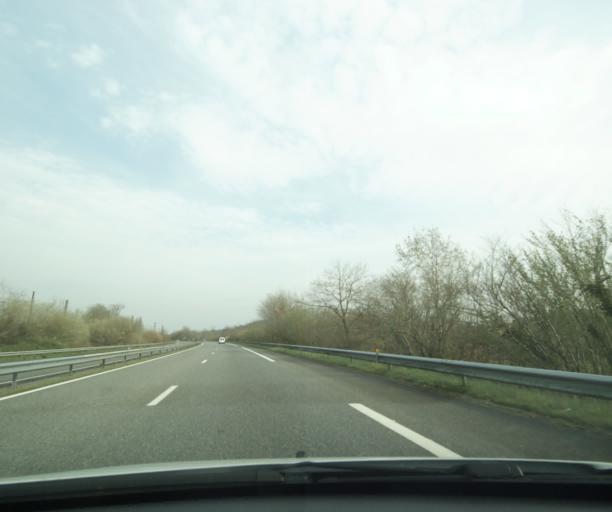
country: FR
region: Aquitaine
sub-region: Departement des Pyrenees-Atlantiques
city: Puyoo
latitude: 43.5061
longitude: -0.8706
